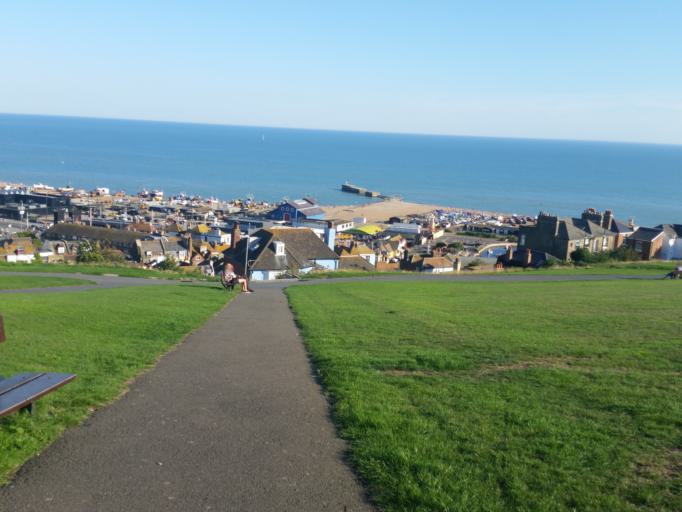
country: GB
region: England
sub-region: East Sussex
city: Hastings
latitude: 50.8580
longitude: 0.5888
